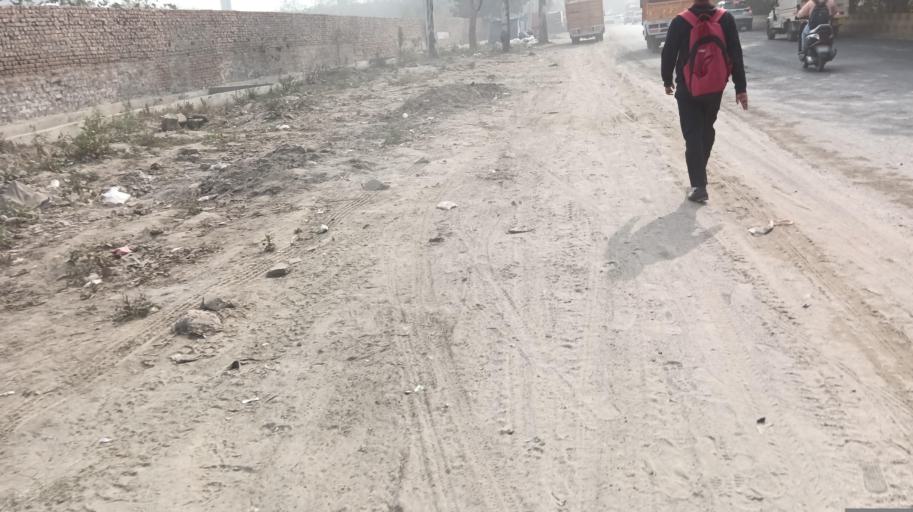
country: IN
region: Uttar Pradesh
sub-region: Ghaziabad
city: Ghaziabad
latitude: 28.6696
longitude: 77.3691
